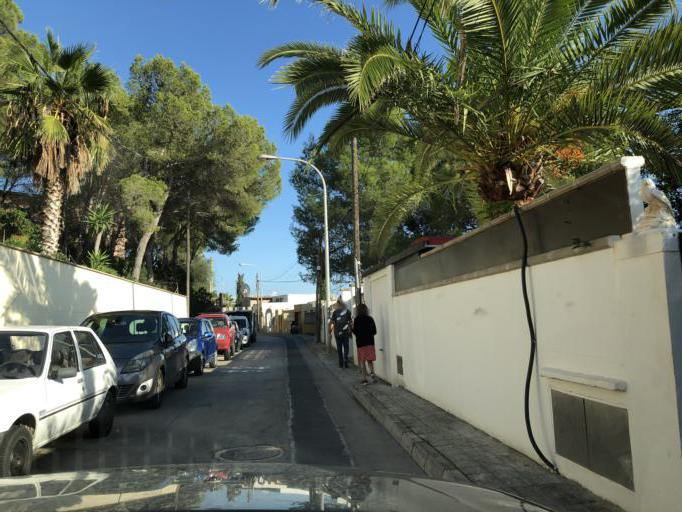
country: ES
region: Balearic Islands
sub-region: Illes Balears
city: Camp de Mar
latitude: 39.5393
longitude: 2.4420
